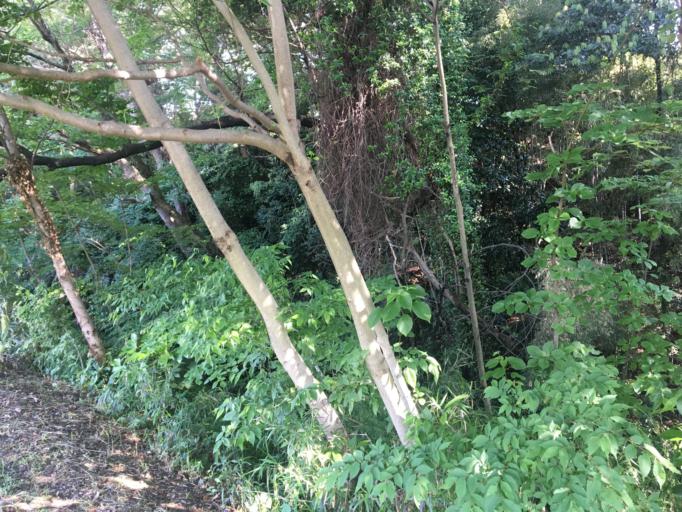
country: JP
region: Saitama
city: Shiki
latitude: 35.8458
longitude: 139.5659
